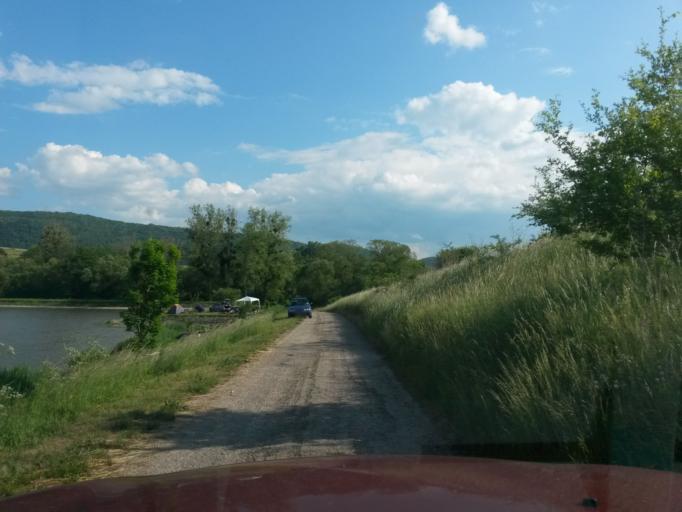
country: SK
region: Kosicky
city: Roznava
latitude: 48.5887
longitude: 20.6442
